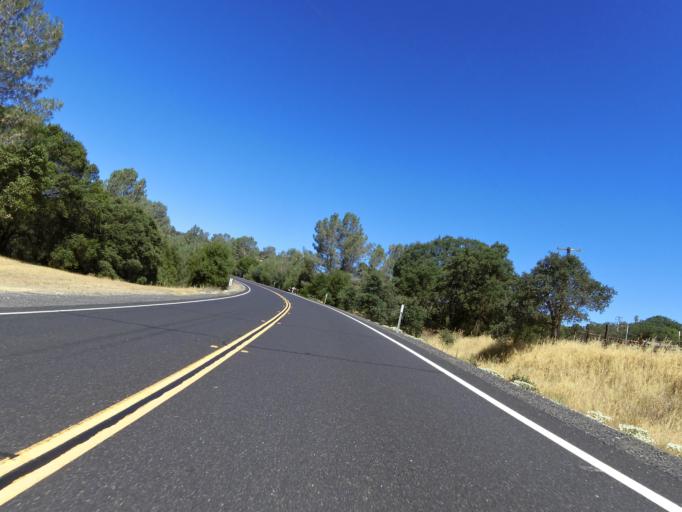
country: US
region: California
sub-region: Tuolumne County
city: Tuolumne City
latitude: 37.7015
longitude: -120.2759
